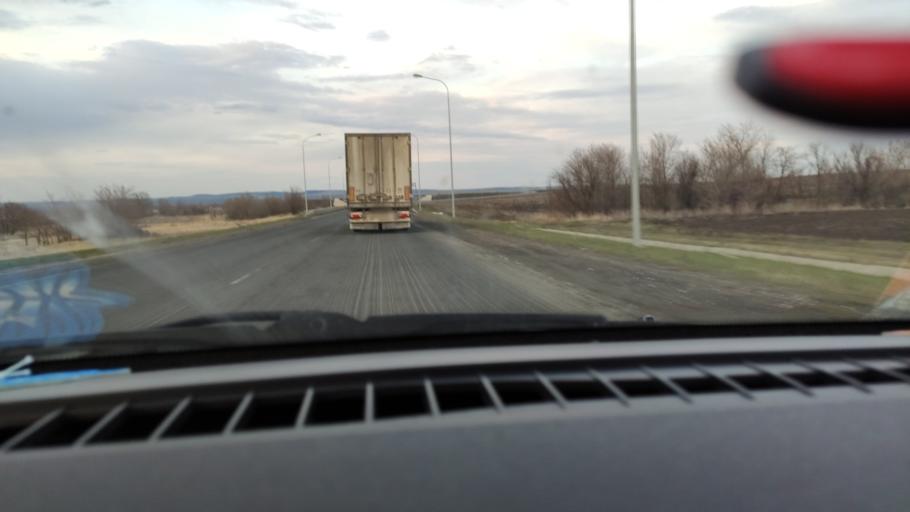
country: RU
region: Saratov
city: Yelshanka
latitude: 51.7960
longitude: 46.1717
